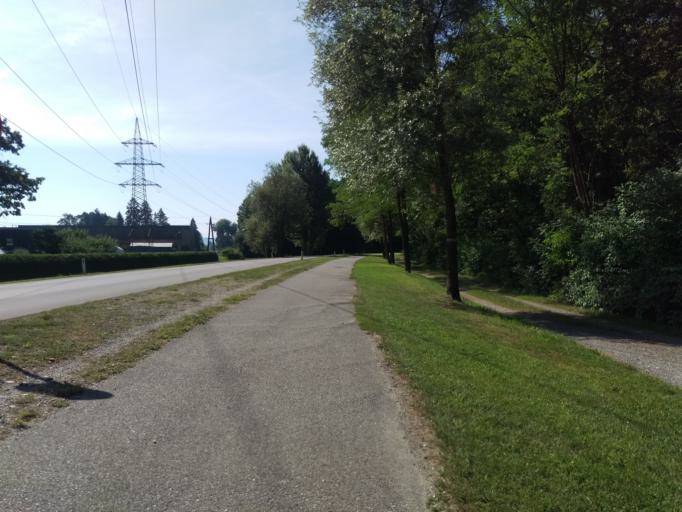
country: AT
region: Styria
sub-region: Politischer Bezirk Graz-Umgebung
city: Feldkirchen bei Graz
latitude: 47.0095
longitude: 15.4677
